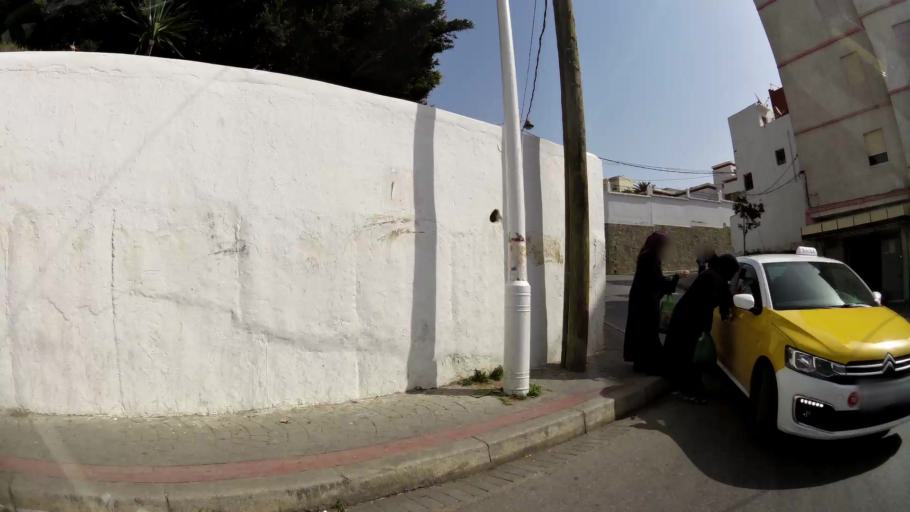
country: MA
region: Tanger-Tetouan
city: Tetouan
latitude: 35.5754
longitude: -5.3790
